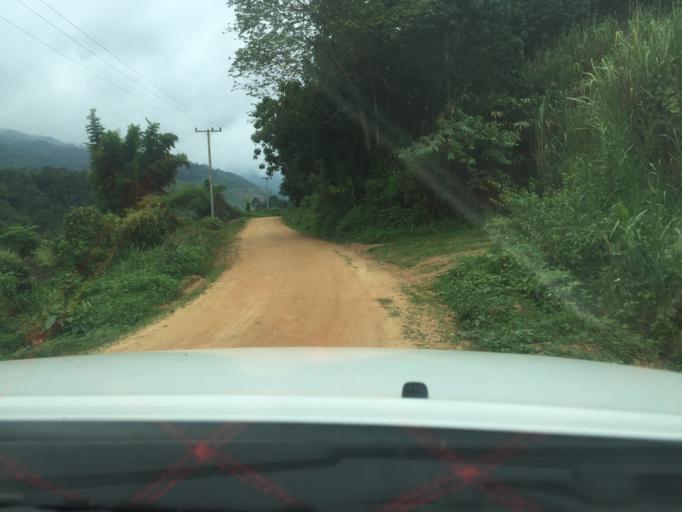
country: TH
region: Phayao
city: Phu Sang
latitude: 19.7365
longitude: 100.4755
